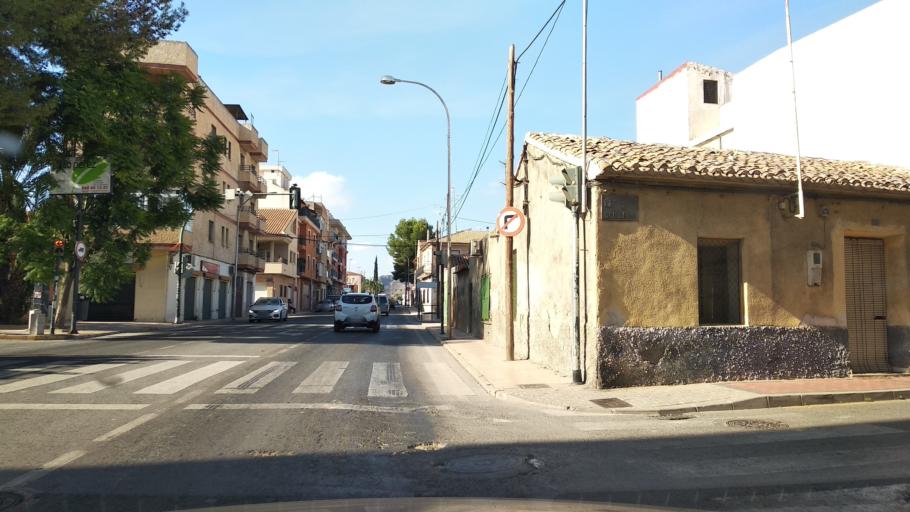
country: ES
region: Murcia
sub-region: Murcia
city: Santomera
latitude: 38.0621
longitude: -1.0535
